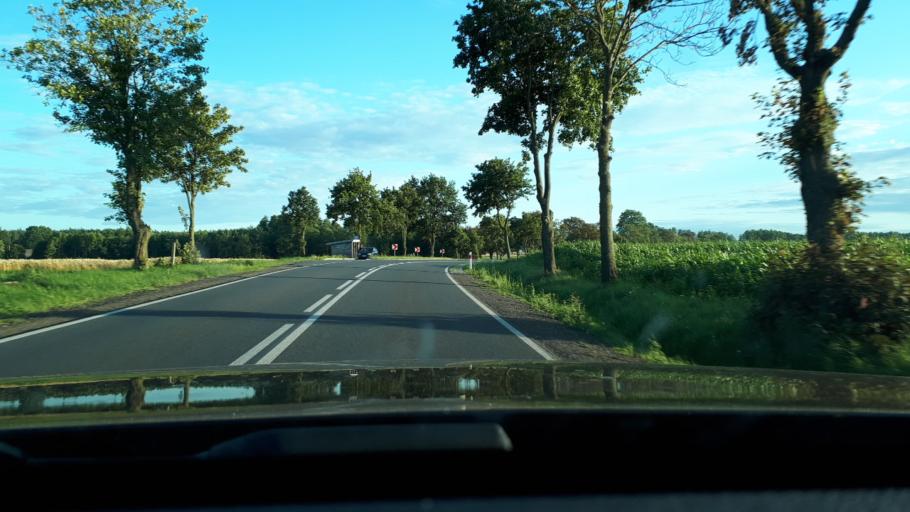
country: PL
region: Masovian Voivodeship
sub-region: Powiat ciechanowski
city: Ciechanow
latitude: 52.8098
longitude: 20.6070
